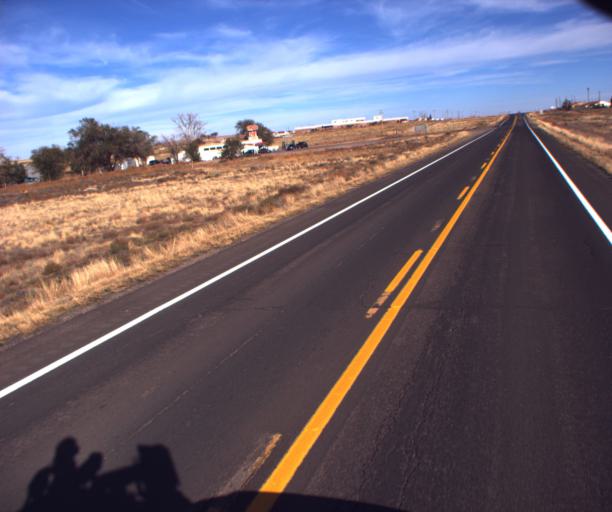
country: US
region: Arizona
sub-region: Apache County
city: Lukachukai
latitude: 36.9600
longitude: -109.3582
